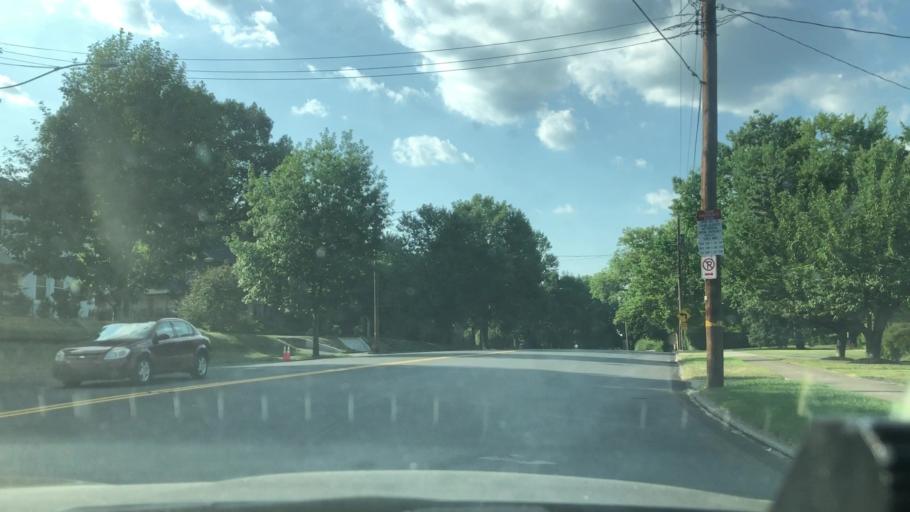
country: US
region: Pennsylvania
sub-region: Lehigh County
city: Fountain Hill
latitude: 40.6262
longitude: -75.4094
